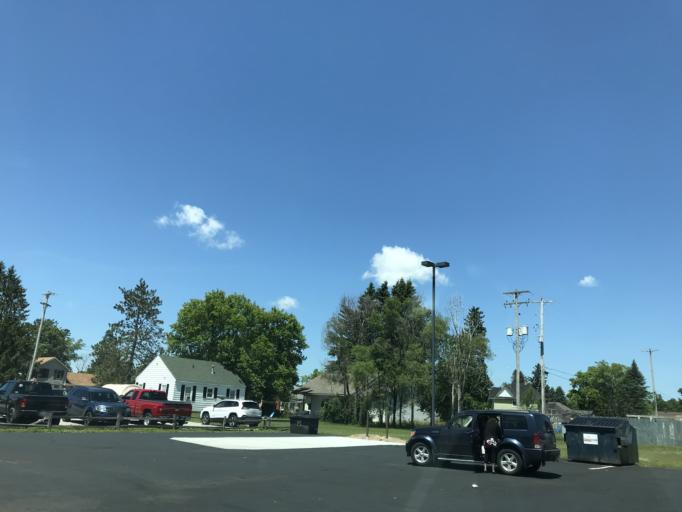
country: US
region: Michigan
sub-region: Otsego County
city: Gaylord
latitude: 45.0278
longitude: -84.6801
